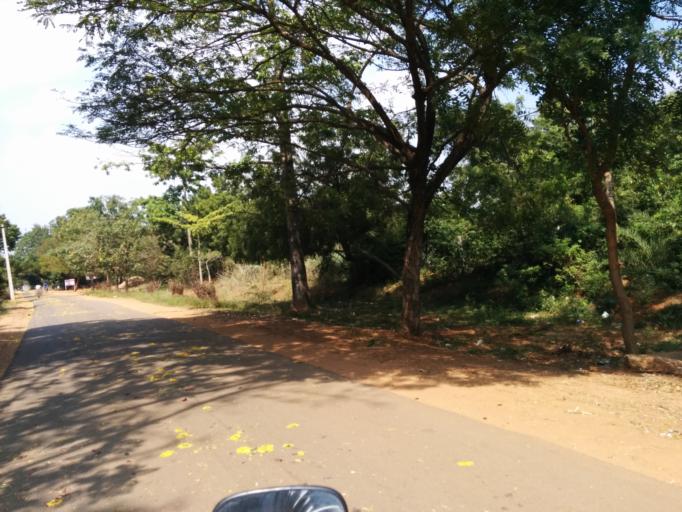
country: IN
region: Tamil Nadu
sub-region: Villupuram
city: Auroville
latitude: 12.0001
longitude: 79.8006
